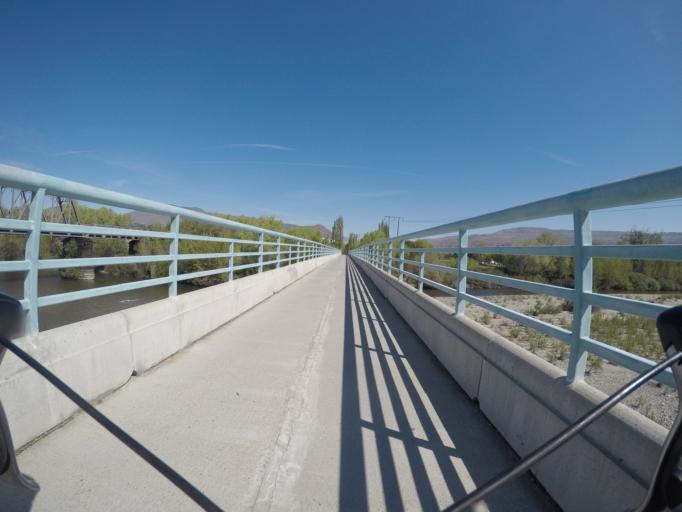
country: US
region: Washington
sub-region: Chelan County
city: Sunnyslope
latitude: 47.4578
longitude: -120.3326
